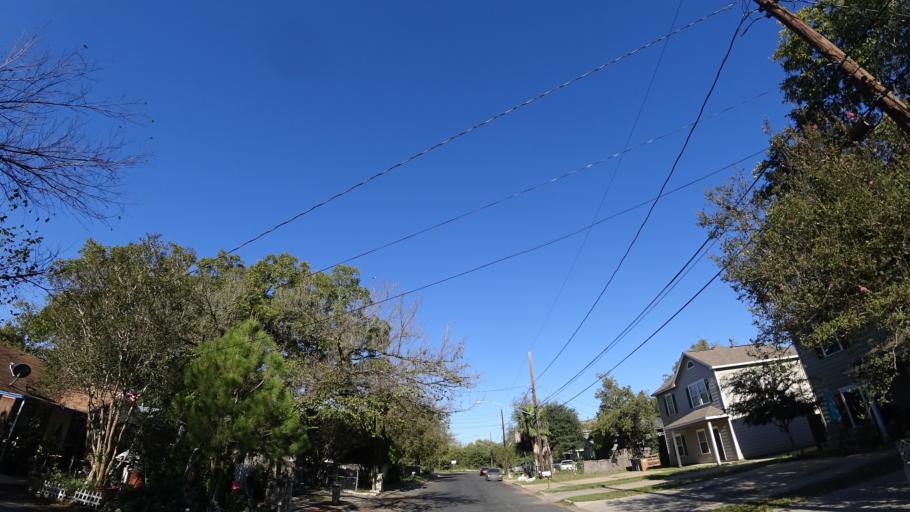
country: US
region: Texas
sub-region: Travis County
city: Austin
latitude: 30.2395
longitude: -97.6972
